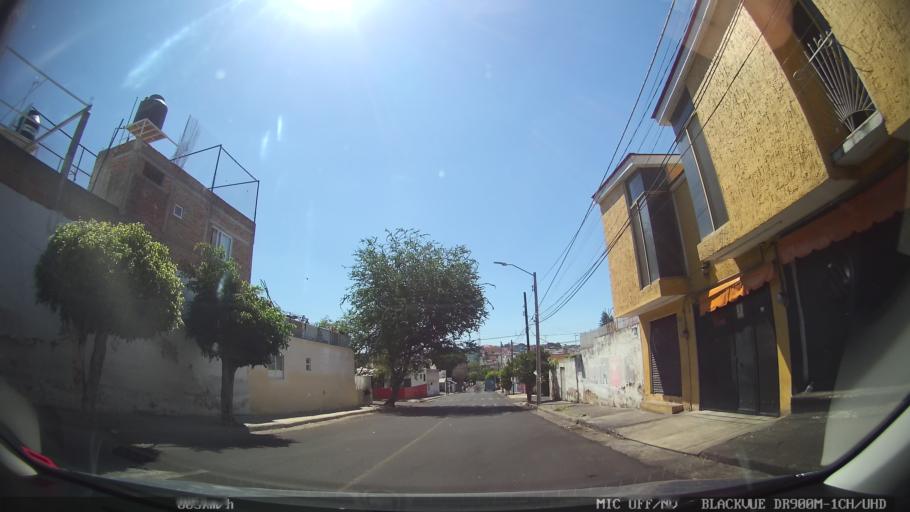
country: MX
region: Jalisco
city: Tlaquepaque
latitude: 20.6950
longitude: -103.2879
